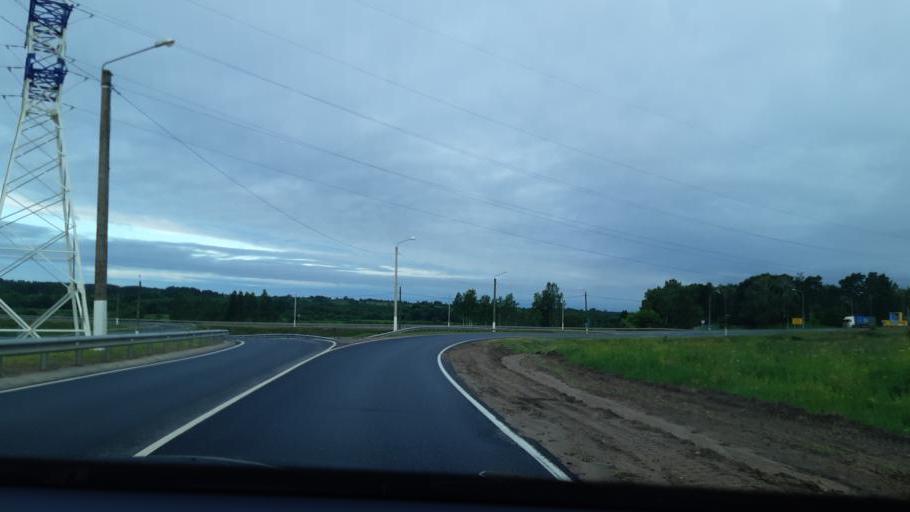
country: RU
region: Smolensk
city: Oster
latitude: 53.9829
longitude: 32.8280
